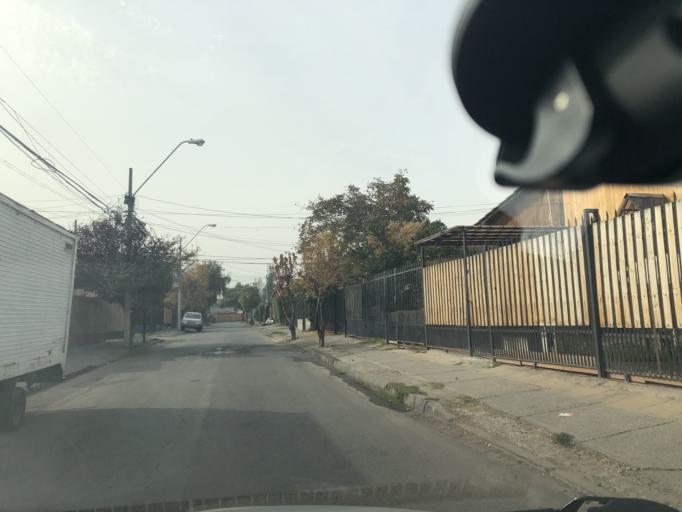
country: CL
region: Santiago Metropolitan
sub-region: Provincia de Cordillera
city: Puente Alto
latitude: -33.5785
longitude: -70.5711
